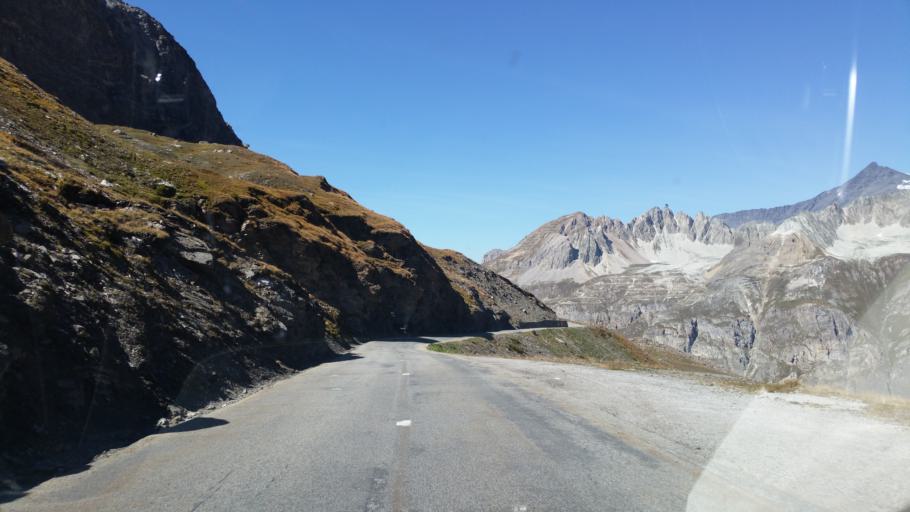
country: FR
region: Rhone-Alpes
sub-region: Departement de la Savoie
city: Val-d'Isere
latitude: 45.4297
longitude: 7.0199
